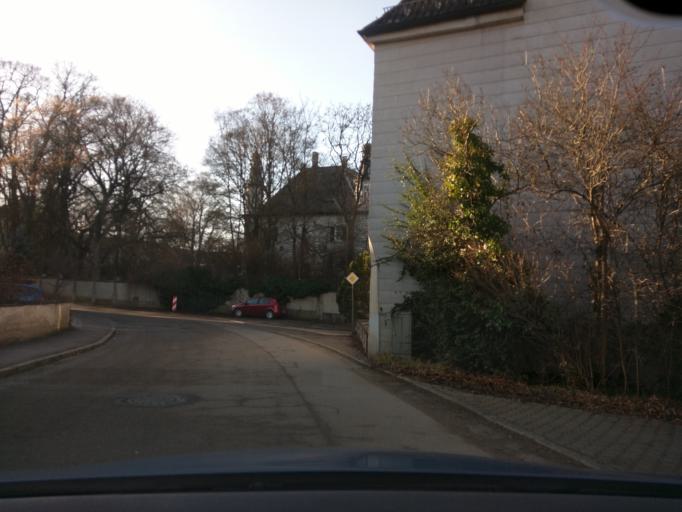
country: DE
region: Bavaria
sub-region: Upper Bavaria
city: Au in der Hallertau
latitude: 48.5585
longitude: 11.7439
